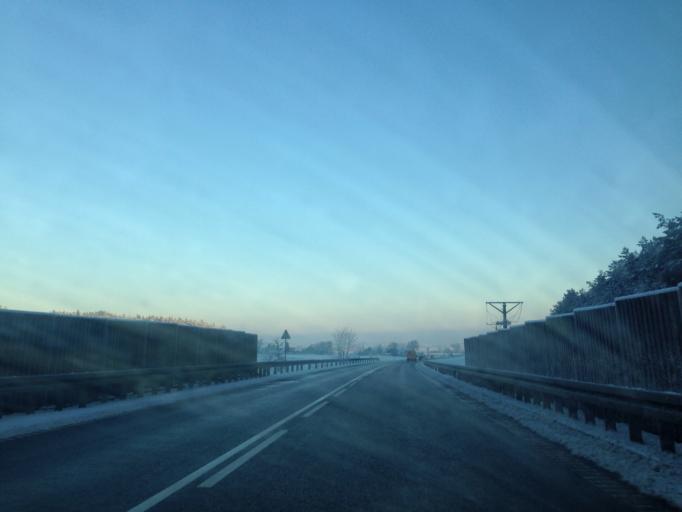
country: PL
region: Pomeranian Voivodeship
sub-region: Powiat tczewski
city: Gniew
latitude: 53.7596
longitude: 18.8098
